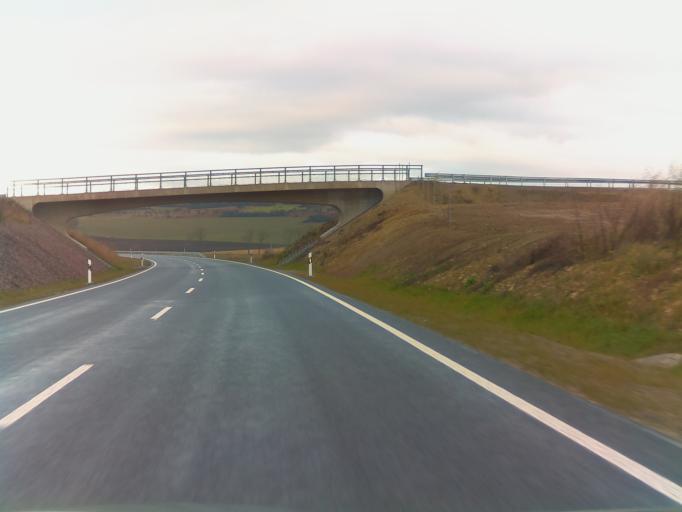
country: DE
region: Thuringia
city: Stadtilm
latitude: 50.7418
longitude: 11.1169
